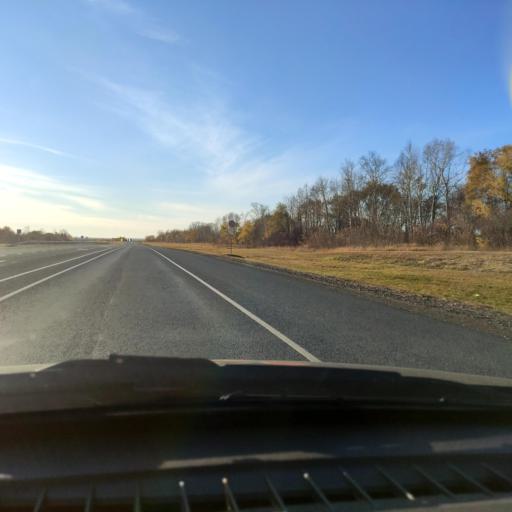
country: RU
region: Samara
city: Balasheyka
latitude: 53.1939
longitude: 48.2414
